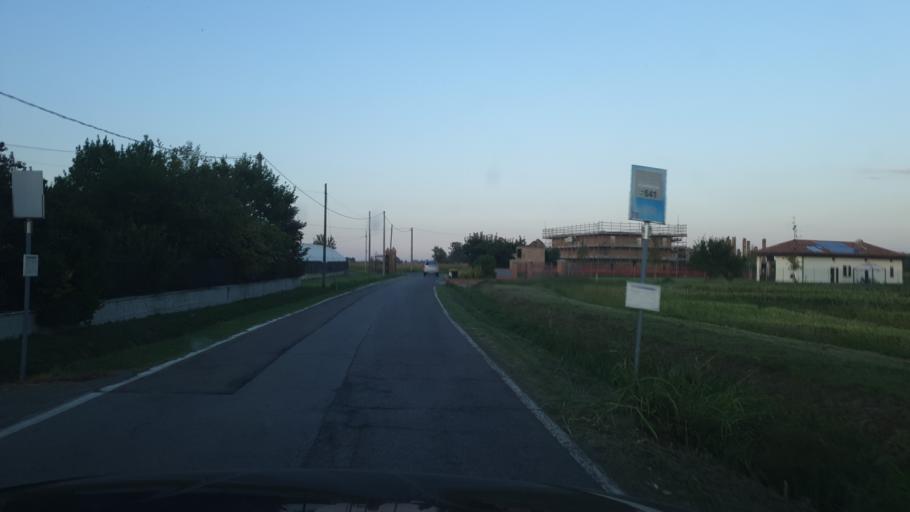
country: IT
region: Emilia-Romagna
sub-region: Provincia di Bologna
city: Progresso
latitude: 44.5799
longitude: 11.3997
